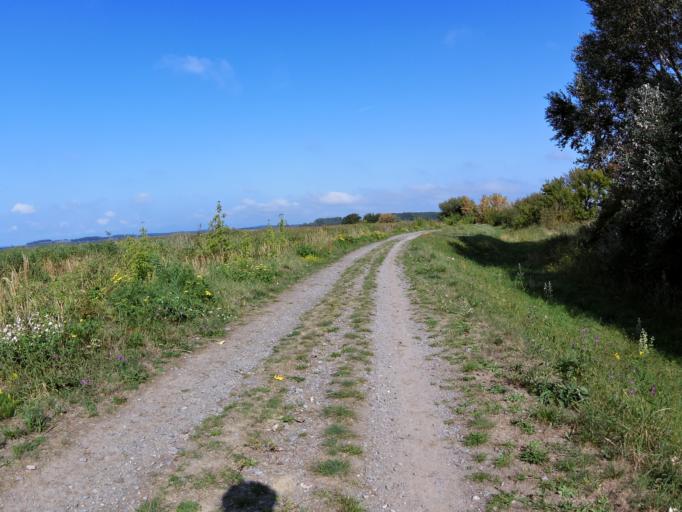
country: DE
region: Mecklenburg-Vorpommern
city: Loddin
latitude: 53.9858
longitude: 14.0487
